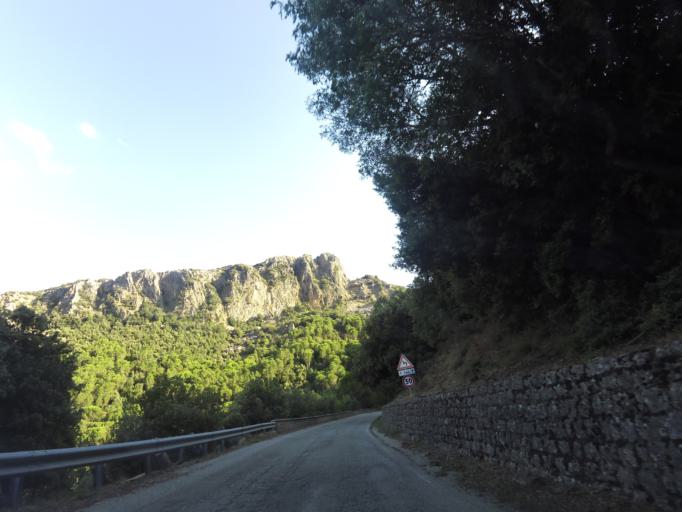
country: IT
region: Calabria
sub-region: Provincia di Reggio Calabria
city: Pazzano
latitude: 38.4651
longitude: 16.4236
